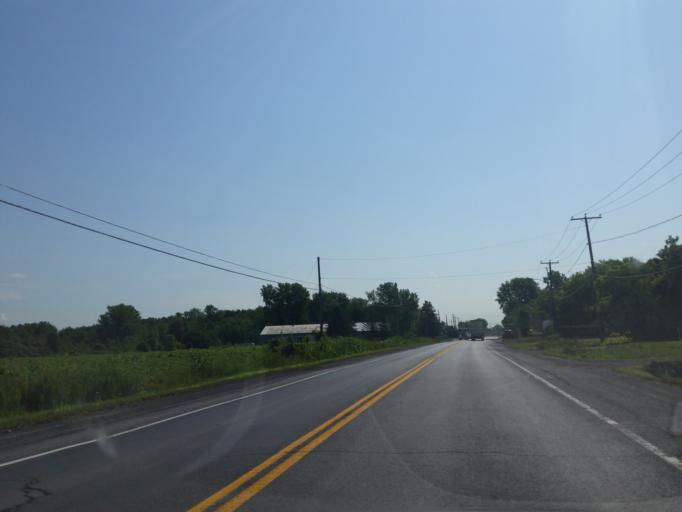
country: CA
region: Quebec
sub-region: Monteregie
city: Saint-Jean-sur-Richelieu
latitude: 45.3034
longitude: -73.3165
